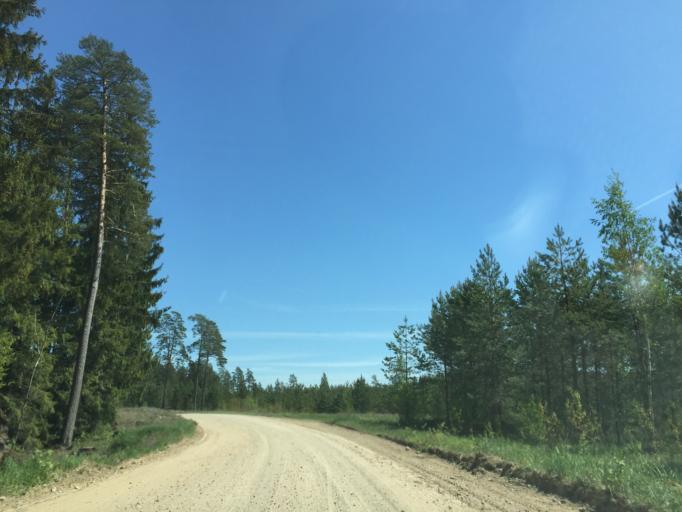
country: LV
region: Ikskile
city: Ikskile
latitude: 56.7323
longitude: 24.5169
